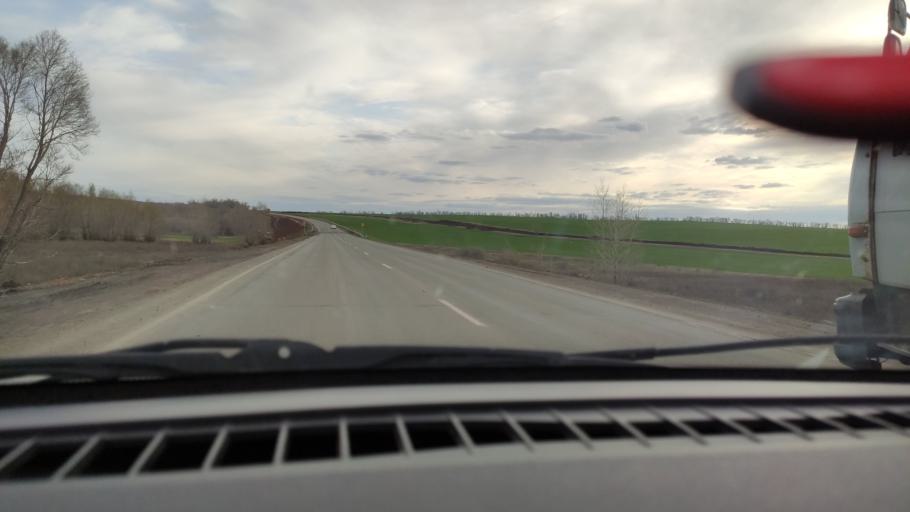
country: RU
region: Orenburg
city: Sakmara
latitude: 52.1886
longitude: 55.2981
